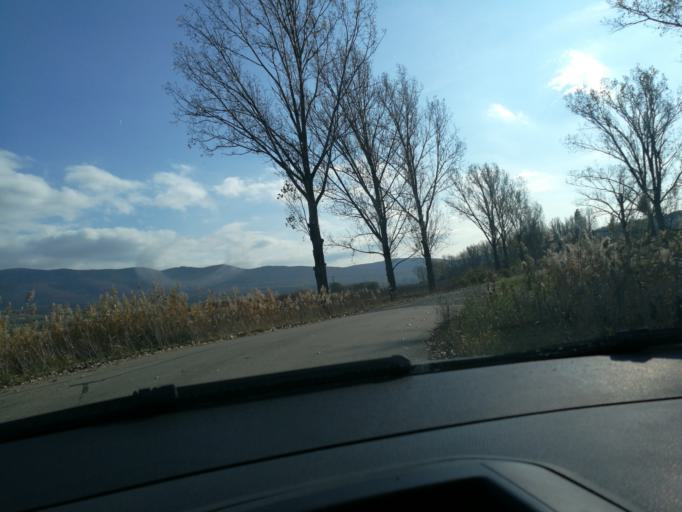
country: HU
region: Nograd
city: Paszto
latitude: 47.9062
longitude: 19.6866
